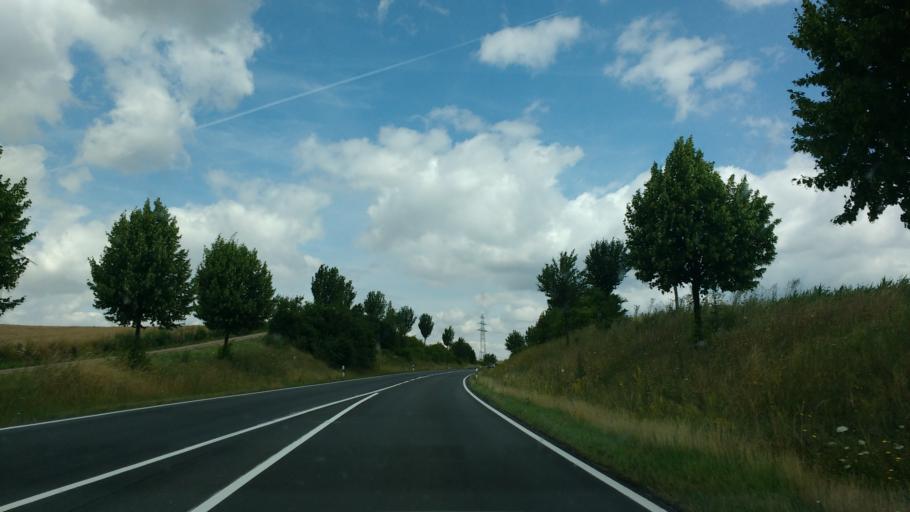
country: DE
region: Saxony-Anhalt
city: Kretzschau
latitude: 51.0484
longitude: 12.0983
